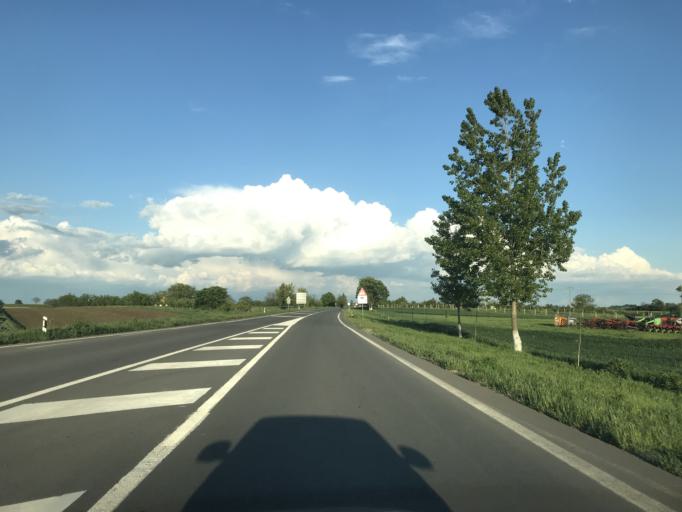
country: RS
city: Aradac
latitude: 45.3917
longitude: 20.2990
